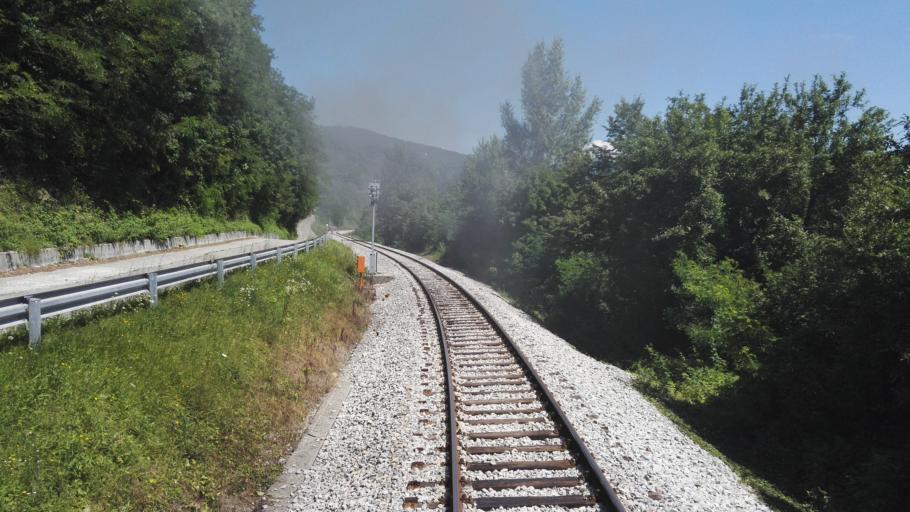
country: SI
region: Kanal
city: Kanal
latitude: 46.0741
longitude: 13.6284
